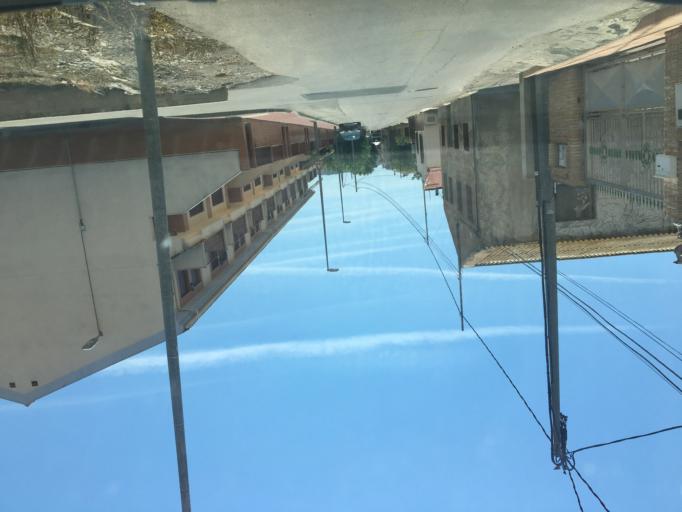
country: ES
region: Murcia
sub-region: Murcia
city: Santomera
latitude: 38.0173
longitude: -1.0548
